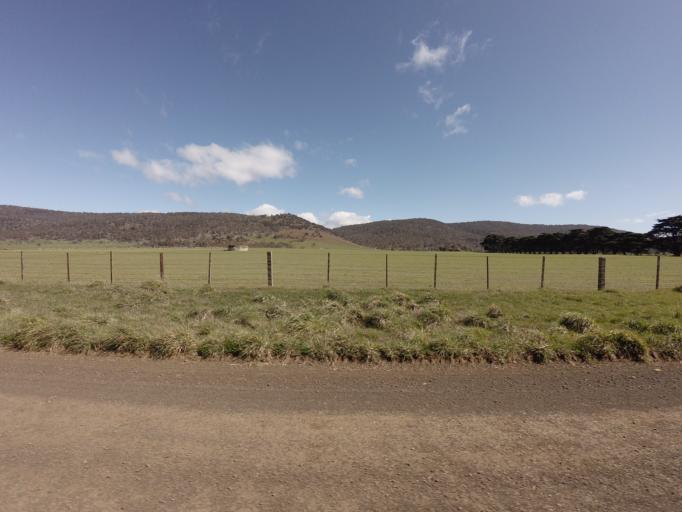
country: AU
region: Tasmania
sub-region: Northern Midlands
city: Evandale
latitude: -41.9515
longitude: 147.4351
